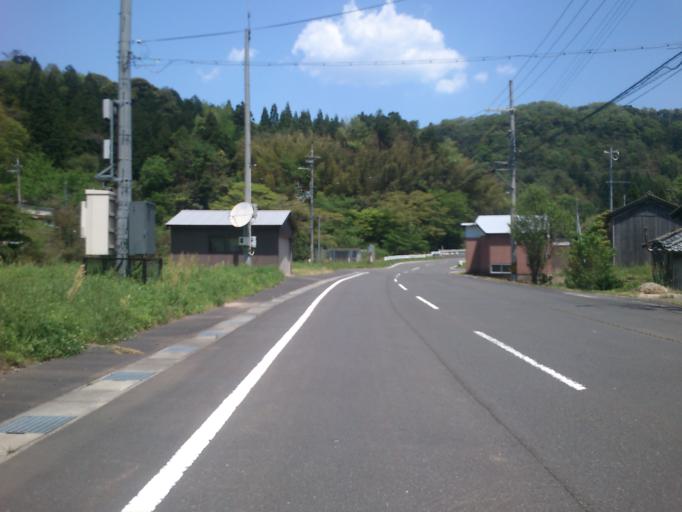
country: JP
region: Kyoto
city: Miyazu
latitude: 35.7277
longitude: 135.1624
